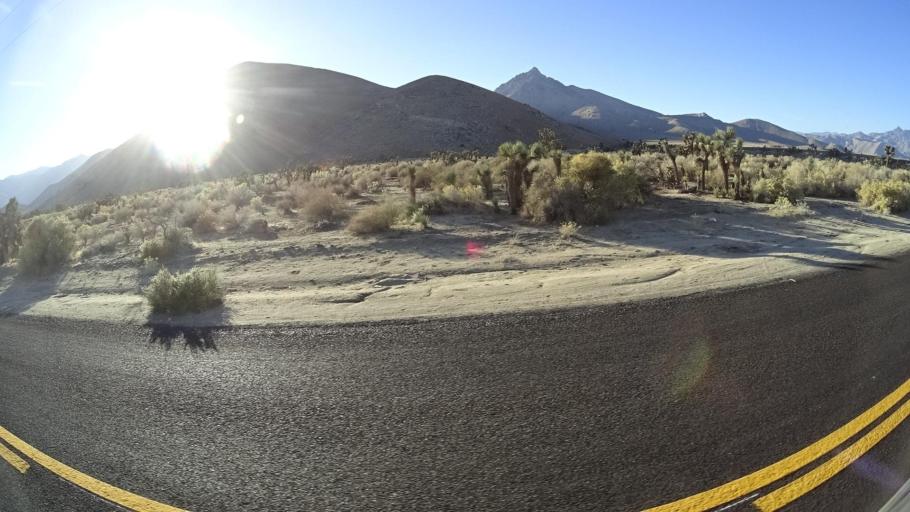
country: US
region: California
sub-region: Kern County
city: Weldon
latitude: 35.6129
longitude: -118.2434
